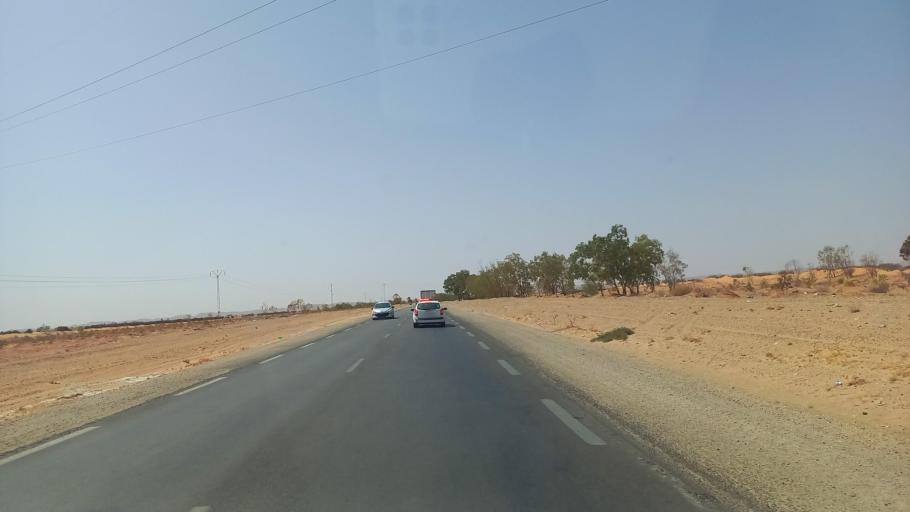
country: TN
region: Madanin
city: Medenine
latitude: 33.2278
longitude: 10.4522
